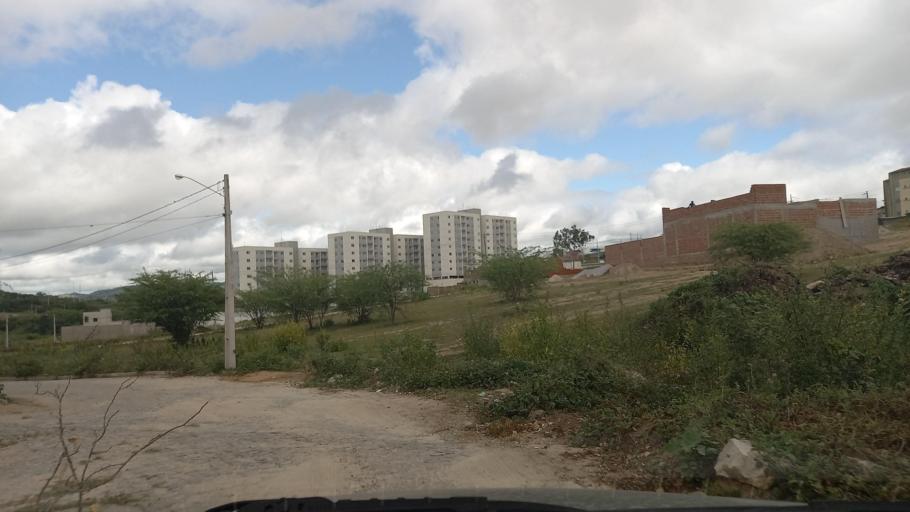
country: BR
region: Pernambuco
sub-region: Caruaru
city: Caruaru
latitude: -8.3025
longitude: -35.9572
